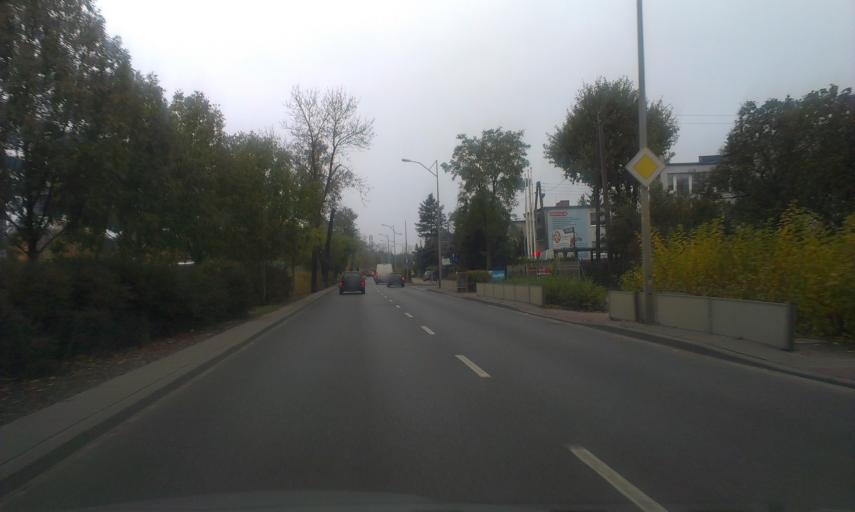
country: PL
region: Greater Poland Voivodeship
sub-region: Powiat poznanski
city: Suchy Las
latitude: 52.4133
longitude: 16.8698
